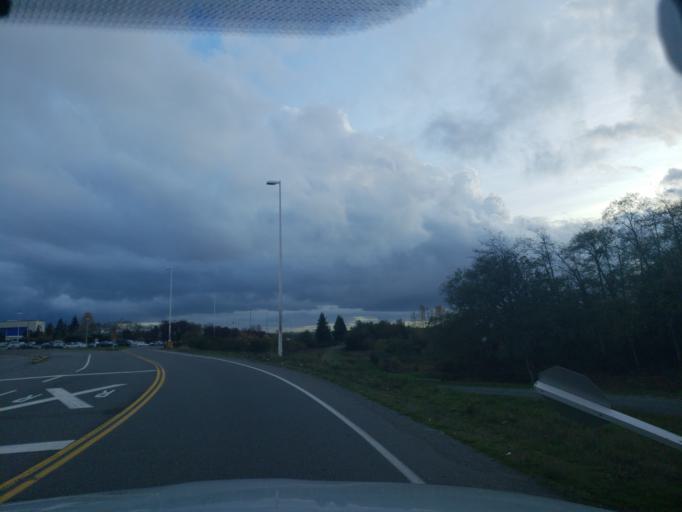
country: US
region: Washington
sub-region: Snohomish County
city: Mukilteo
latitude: 47.9275
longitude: -122.2851
